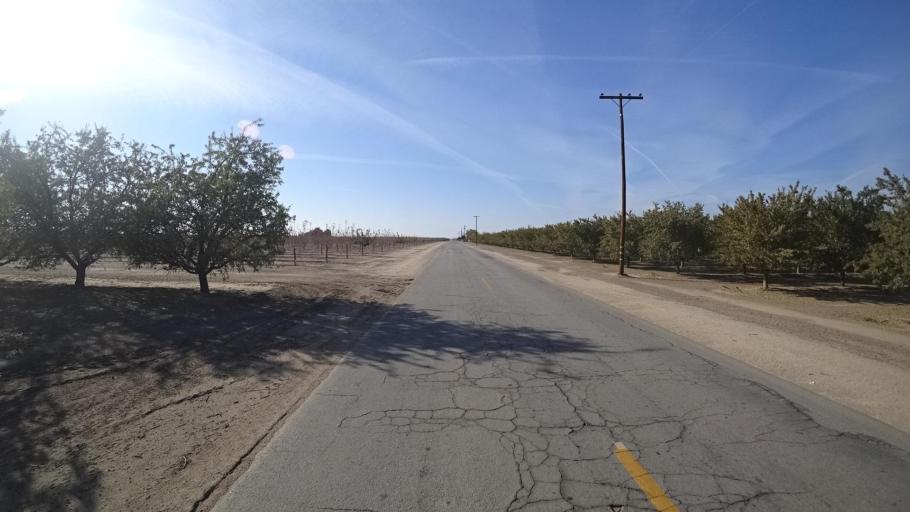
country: US
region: California
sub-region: Kern County
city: McFarland
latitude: 35.7032
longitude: -119.2985
